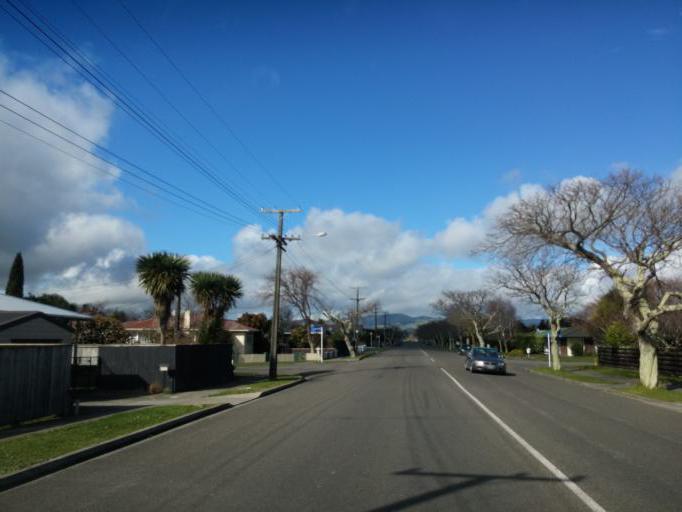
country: NZ
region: Manawatu-Wanganui
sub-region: Palmerston North City
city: Palmerston North
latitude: -40.3714
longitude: 175.5787
